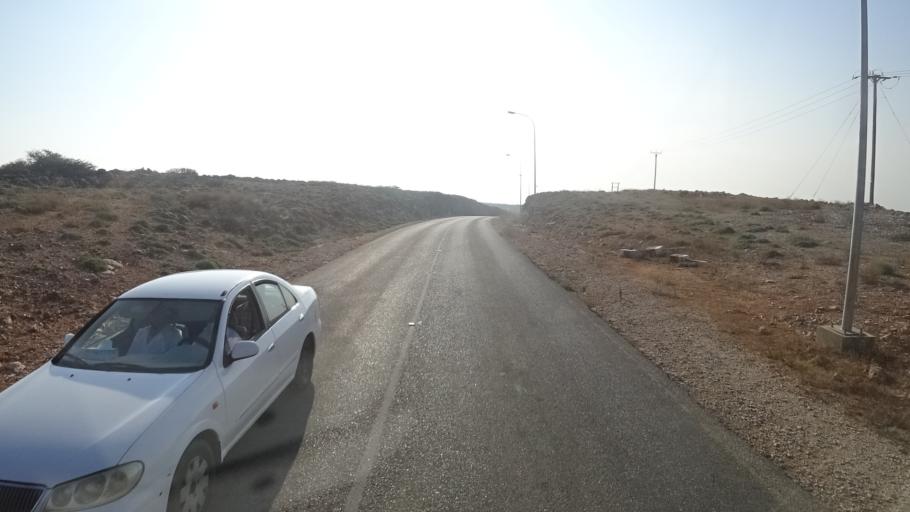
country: YE
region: Al Mahrah
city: Hawf
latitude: 16.7621
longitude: 53.2342
